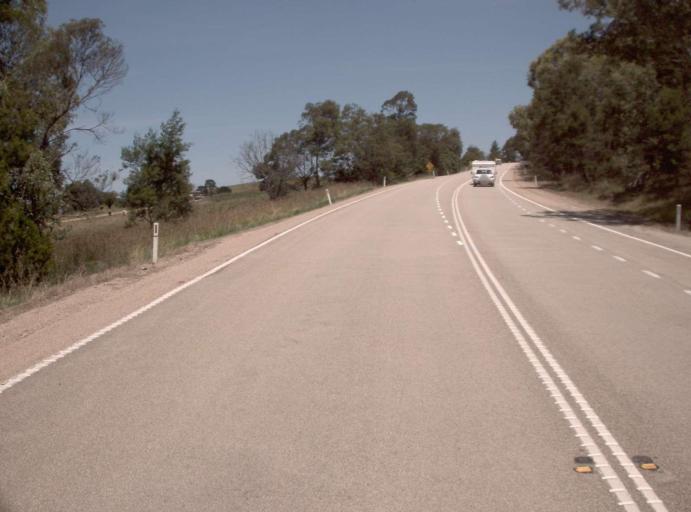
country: AU
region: Victoria
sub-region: East Gippsland
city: Bairnsdale
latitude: -37.7207
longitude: 147.8046
